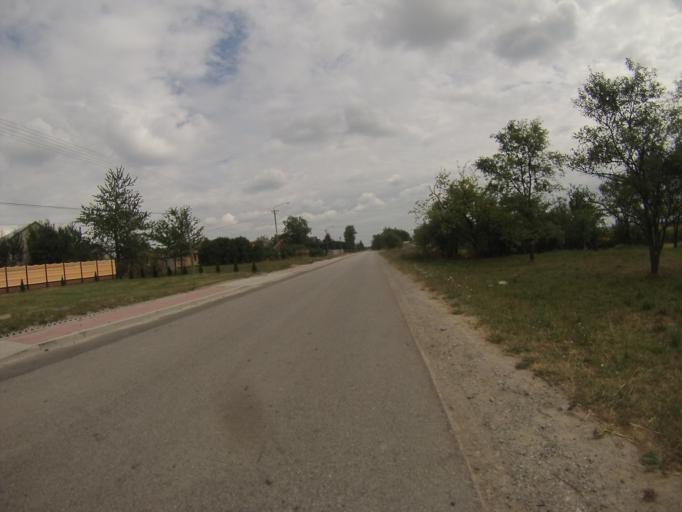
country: PL
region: Swietokrzyskie
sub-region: Powiat kielecki
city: Lagow
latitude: 50.7328
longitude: 21.0872
